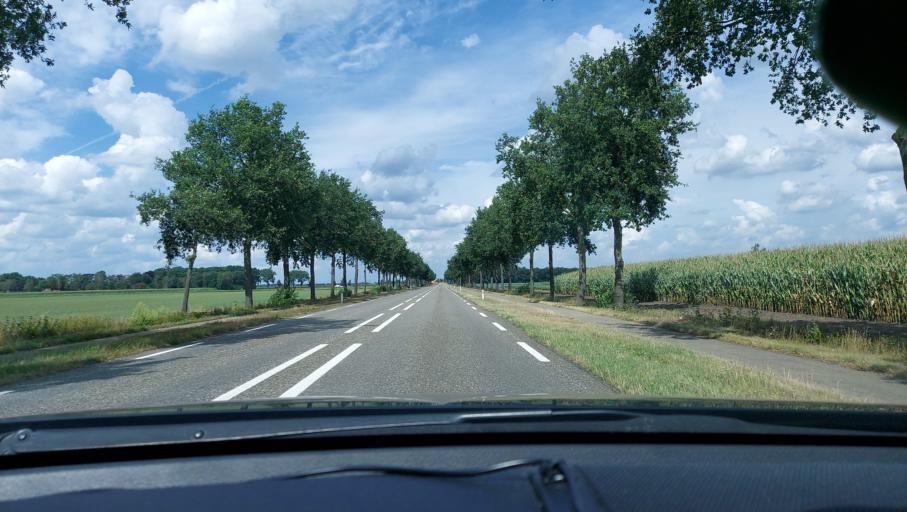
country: NL
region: Limburg
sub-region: Gemeente Peel en Maas
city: Maasbree
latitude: 51.4017
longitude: 5.9685
